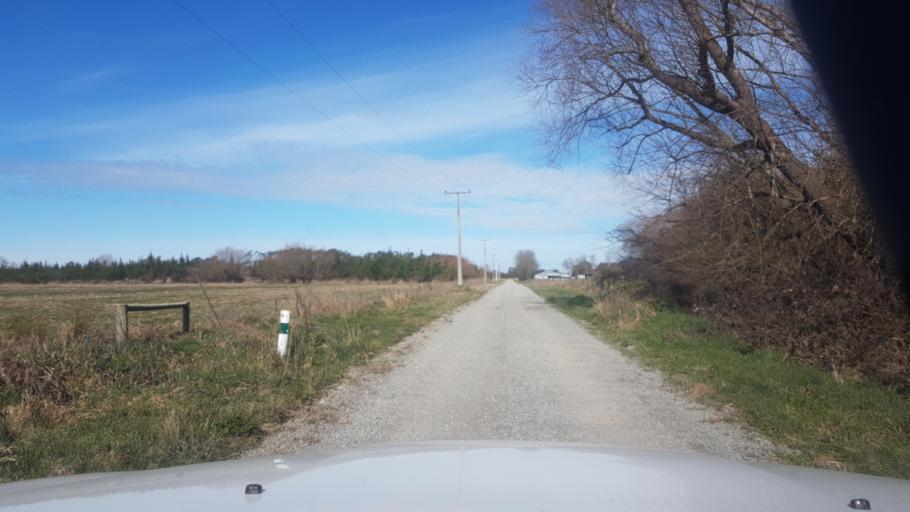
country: NZ
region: Canterbury
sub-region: Timaru District
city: Pleasant Point
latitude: -44.1325
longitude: 171.2739
